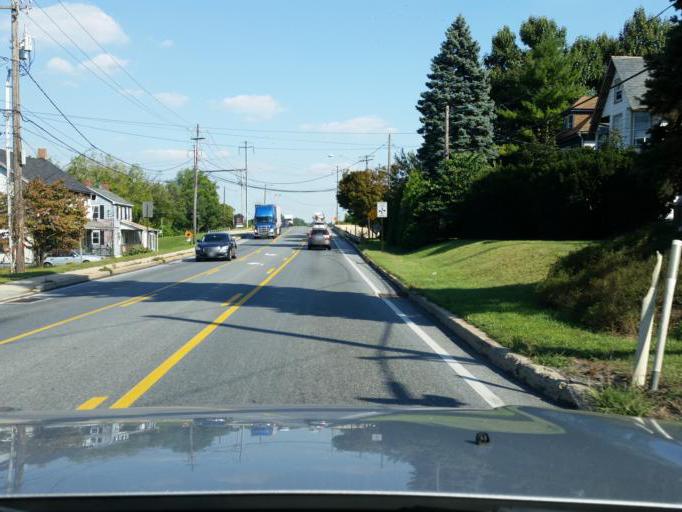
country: US
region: Pennsylvania
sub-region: Lancaster County
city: Paradise
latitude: 40.0077
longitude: -76.1189
